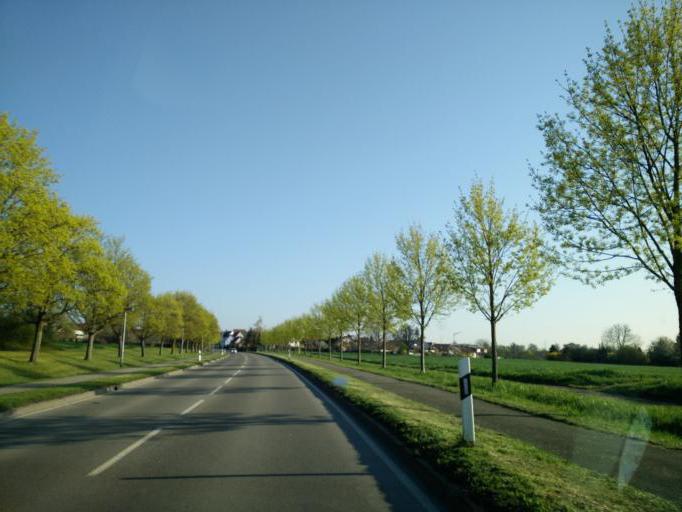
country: DE
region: Baden-Wuerttemberg
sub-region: Regierungsbezirk Stuttgart
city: Herrenberg
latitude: 48.6018
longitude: 8.8605
